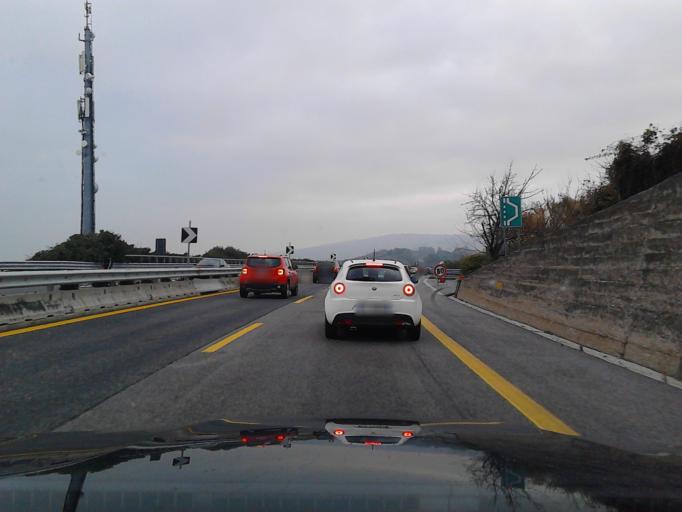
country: IT
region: Abruzzo
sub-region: Provincia di Teramo
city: Tortoreto Lido
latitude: 42.7936
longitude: 13.9338
